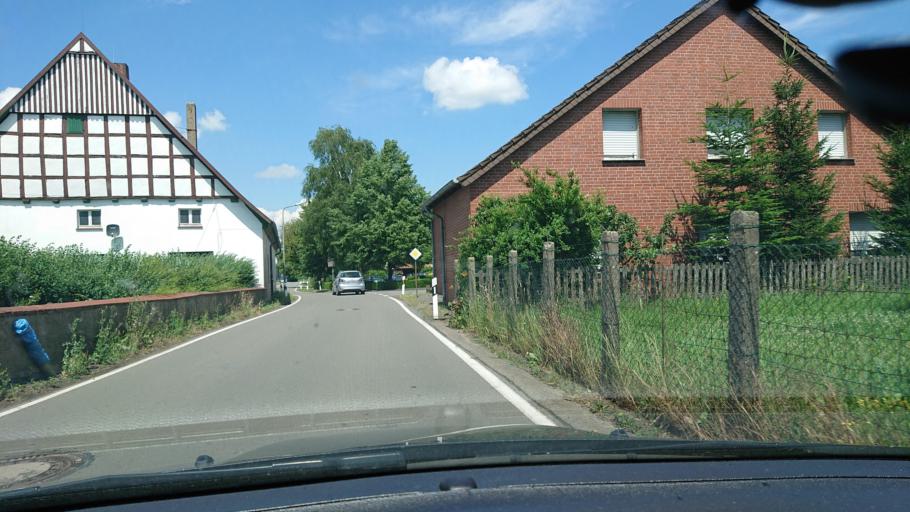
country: DE
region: North Rhine-Westphalia
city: Preussisch Oldendorf
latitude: 52.3114
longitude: 8.4850
